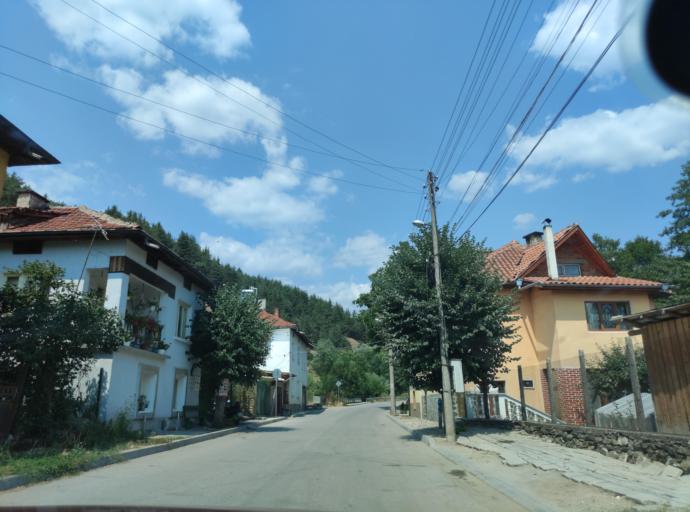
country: BG
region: Blagoevgrad
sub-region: Obshtina Belitsa
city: Belitsa
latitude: 41.9533
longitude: 23.5564
